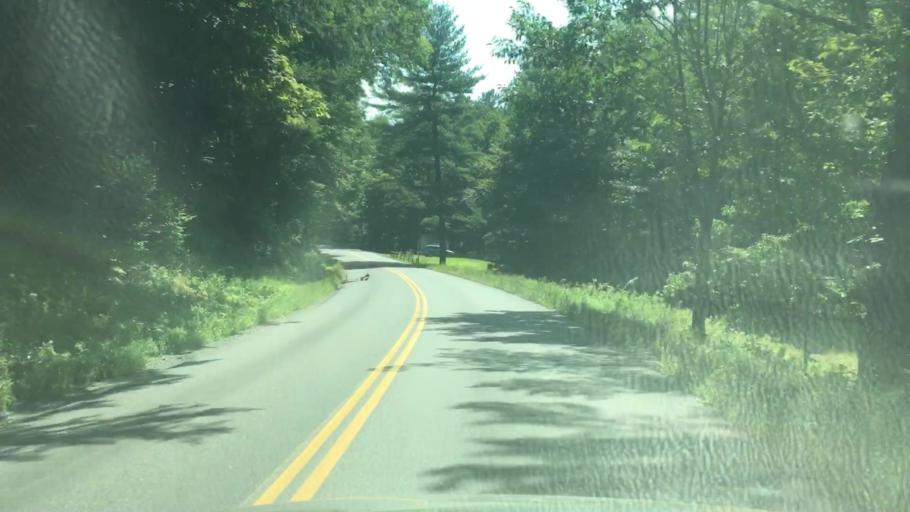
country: US
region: Vermont
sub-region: Windham County
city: West Brattleboro
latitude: 42.8066
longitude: -72.6092
